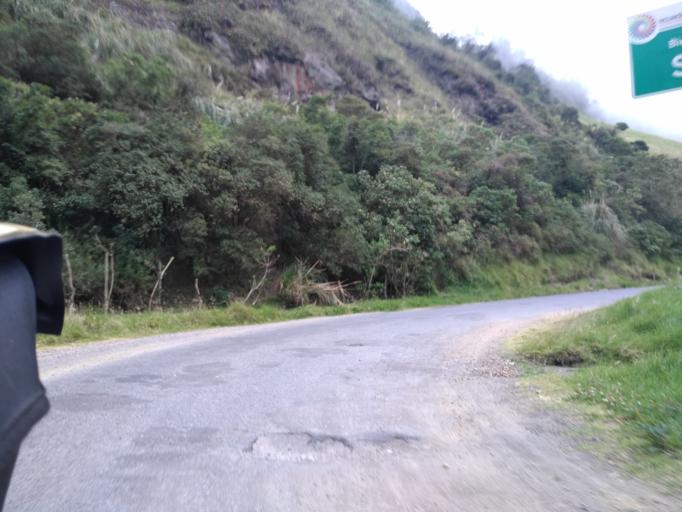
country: EC
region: Cotopaxi
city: Saquisili
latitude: -0.6975
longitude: -78.8112
